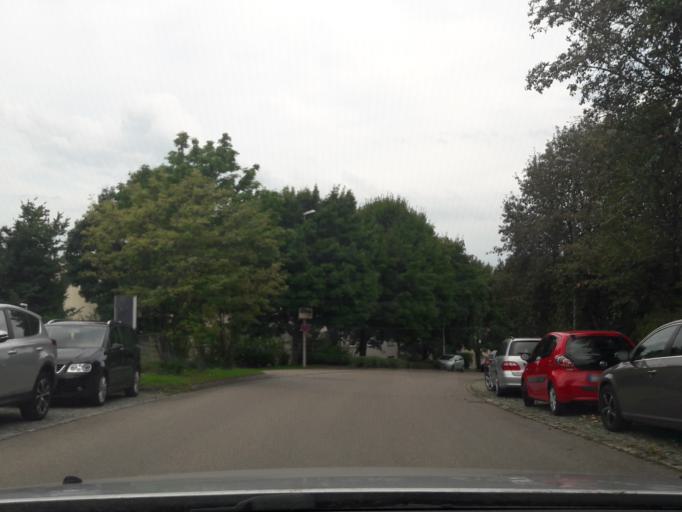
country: DE
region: Baden-Wuerttemberg
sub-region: Regierungsbezirk Stuttgart
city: Backnang
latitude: 48.9594
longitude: 9.4280
